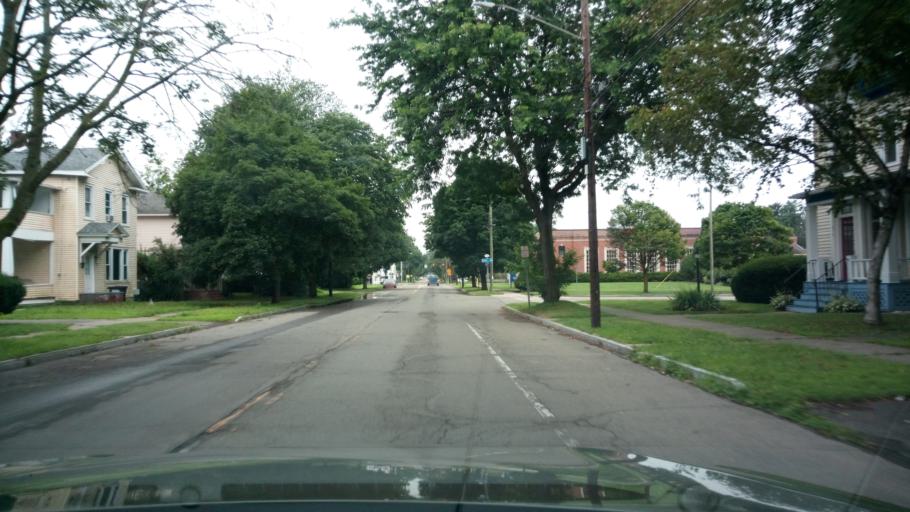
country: US
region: New York
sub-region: Chemung County
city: Elmira
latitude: 42.0862
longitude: -76.8205
